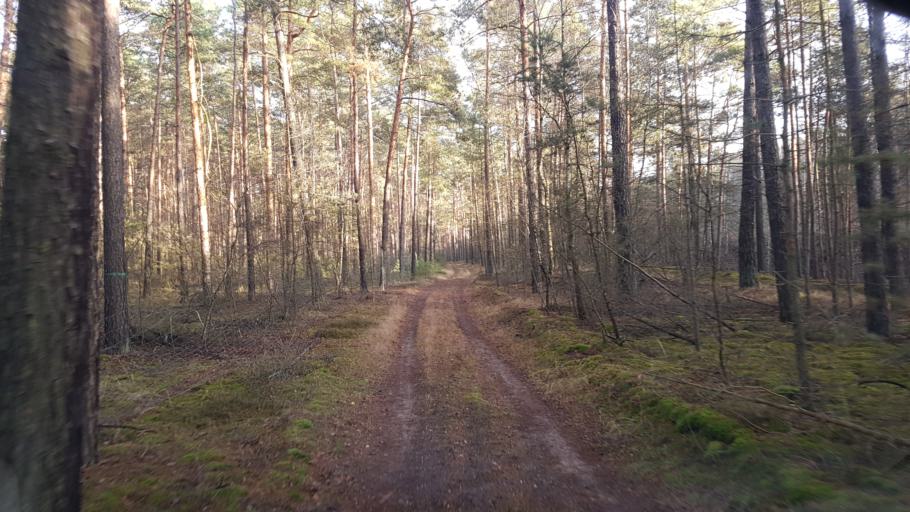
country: DE
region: Brandenburg
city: Finsterwalde
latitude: 51.6283
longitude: 13.6540
